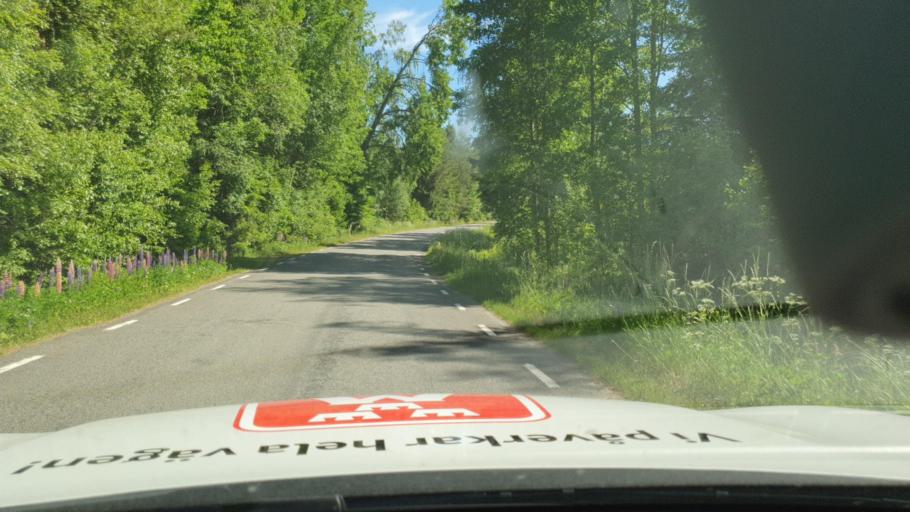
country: SE
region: Vaestra Goetaland
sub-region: Tidaholms Kommun
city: Olofstorp
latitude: 58.2790
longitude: 13.9816
